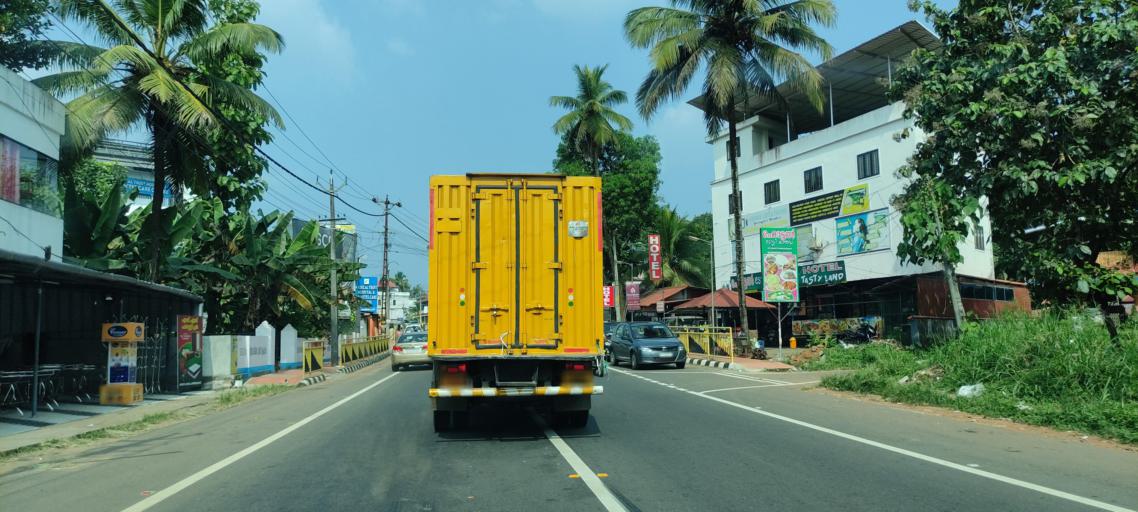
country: IN
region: Kerala
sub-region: Pattanamtitta
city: Adur
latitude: 9.2392
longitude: 76.6720
